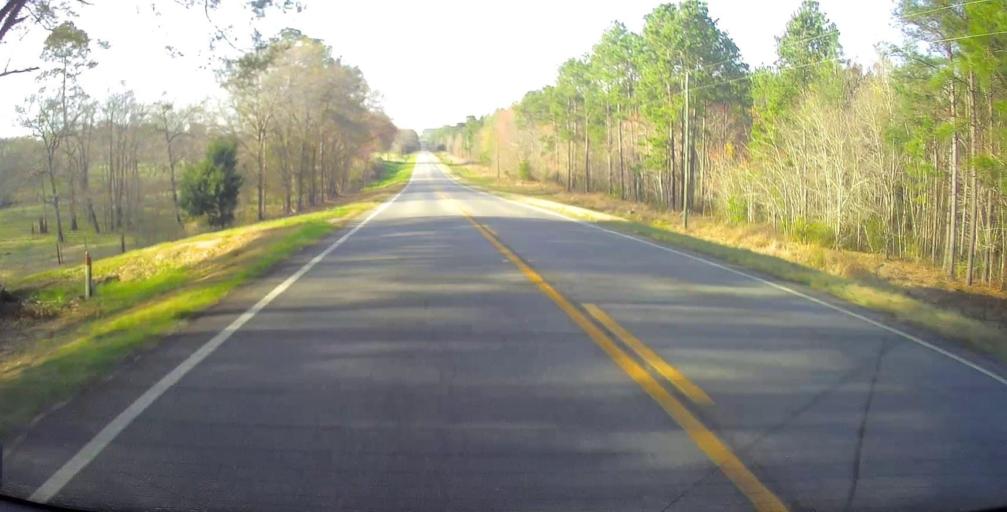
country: US
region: Georgia
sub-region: Toombs County
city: Lyons
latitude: 32.1607
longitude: -82.2695
